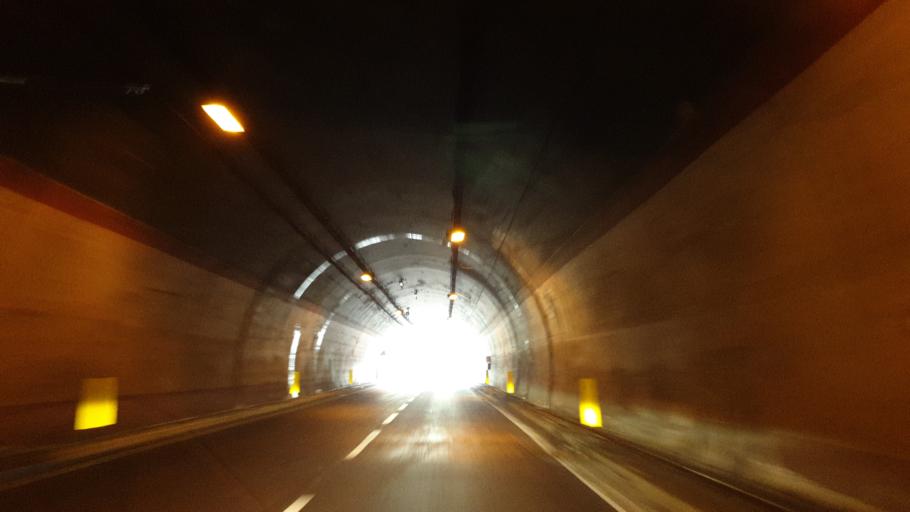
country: IT
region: Emilia-Romagna
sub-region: Forli-Cesena
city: Sarsina
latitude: 43.8911
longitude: 12.0762
